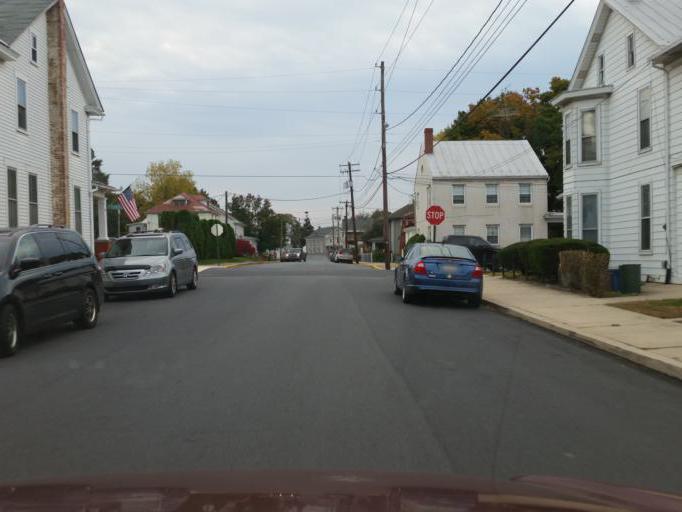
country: US
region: Pennsylvania
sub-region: Dauphin County
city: Hummelstown
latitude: 40.2641
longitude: -76.7073
